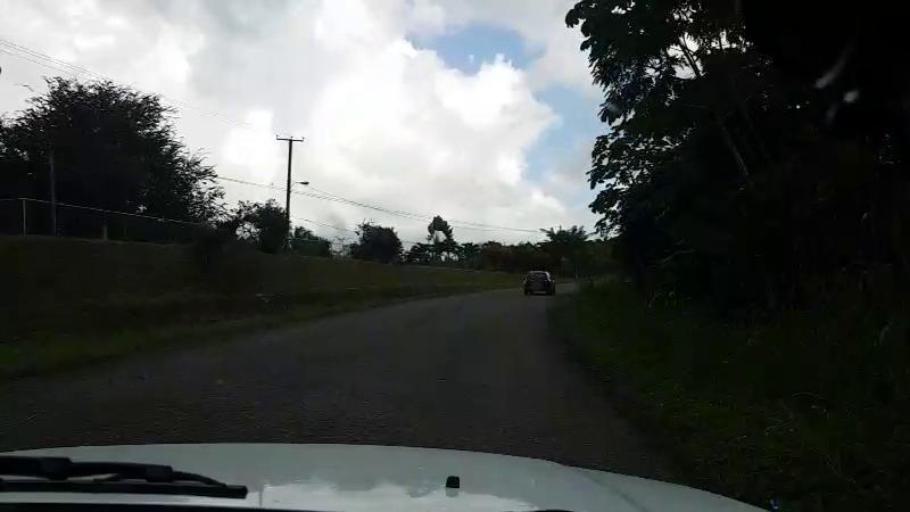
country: BZ
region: Stann Creek
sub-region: Dangriga
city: Dangriga
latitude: 17.0046
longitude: -88.4364
